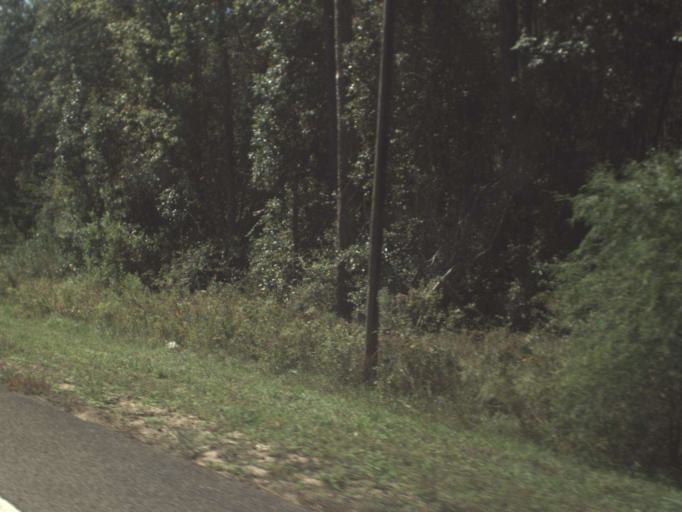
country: US
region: Florida
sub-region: Walton County
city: DeFuniak Springs
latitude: 30.8885
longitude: -86.1269
